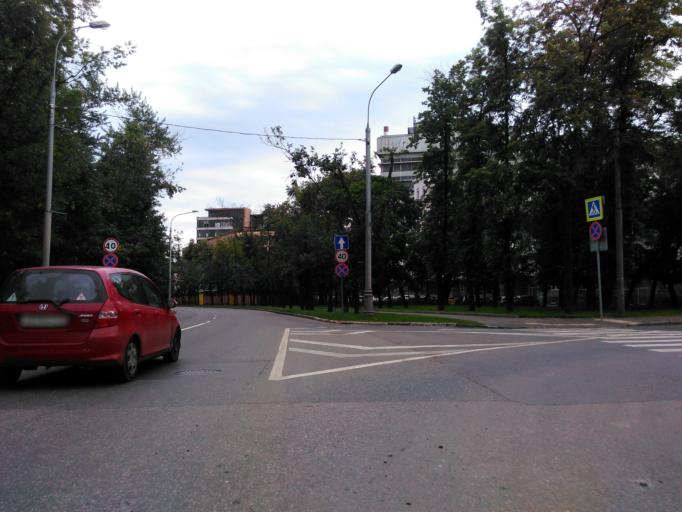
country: RU
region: Moscow
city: Taganskiy
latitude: 55.7559
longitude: 37.6700
